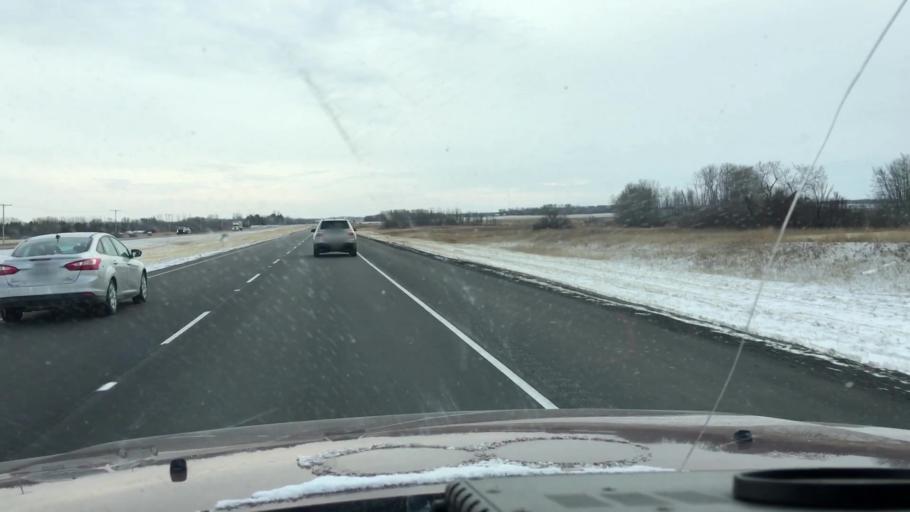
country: CA
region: Saskatchewan
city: Saskatoon
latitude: 52.0234
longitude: -106.5799
